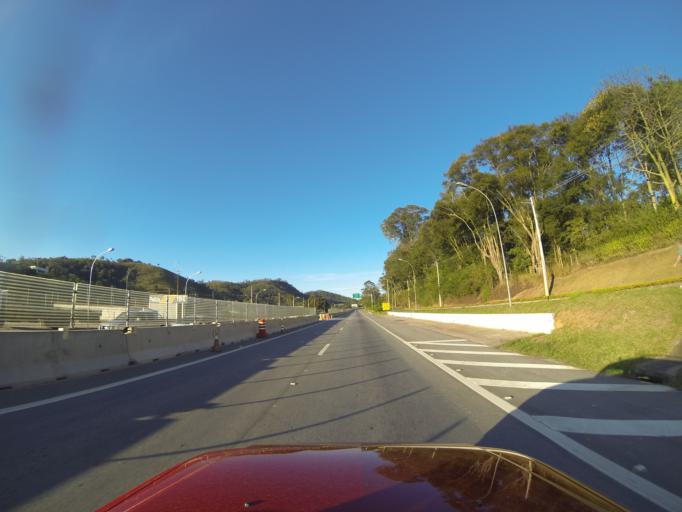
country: BR
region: Sao Paulo
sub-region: Santa Branca
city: Santa Branca
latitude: -23.3200
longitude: -45.7354
